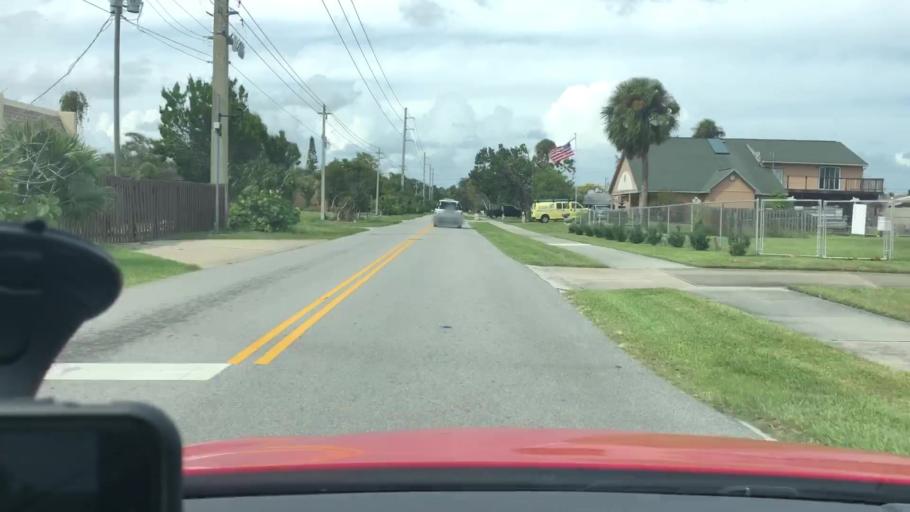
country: US
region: Florida
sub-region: Volusia County
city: South Daytona
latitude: 29.1808
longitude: -81.0050
